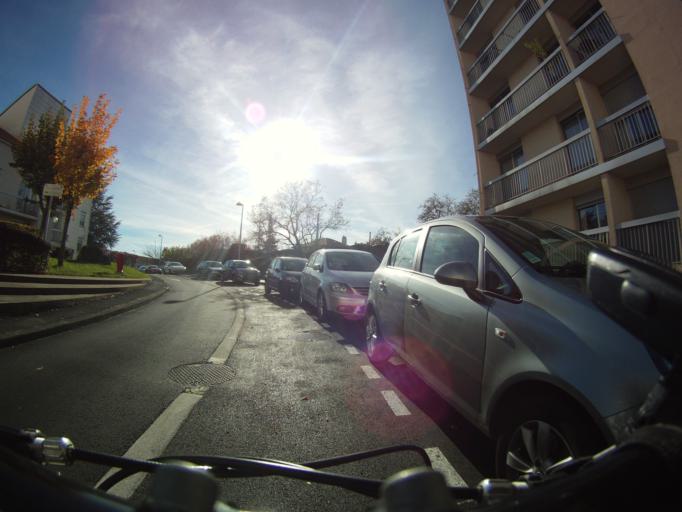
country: FR
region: Auvergne
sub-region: Departement du Puy-de-Dome
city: Beaumont
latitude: 45.7538
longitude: 3.0930
